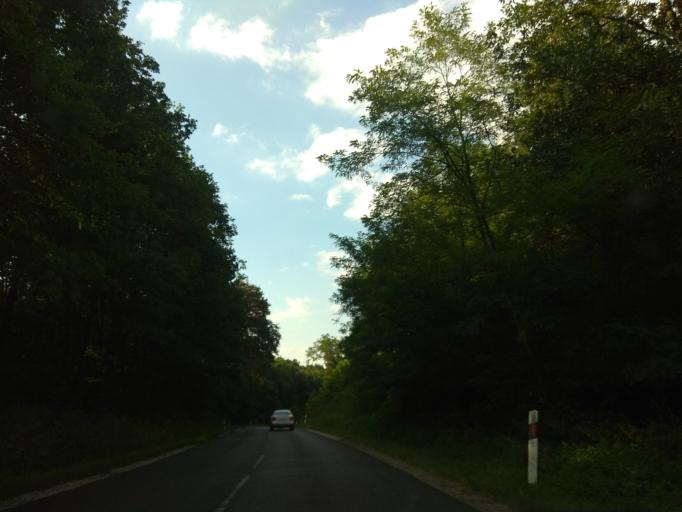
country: HU
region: Borsod-Abauj-Zemplen
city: Harsany
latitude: 47.9931
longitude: 20.7540
